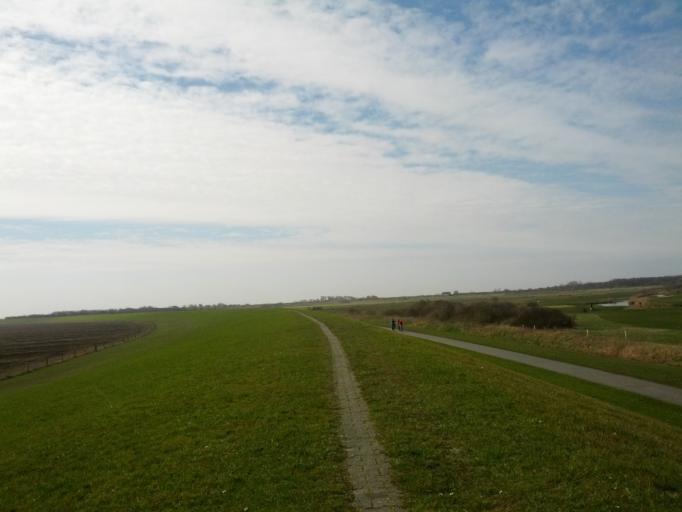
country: DE
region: Lower Saxony
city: Langeoog
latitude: 53.7411
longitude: 7.5040
